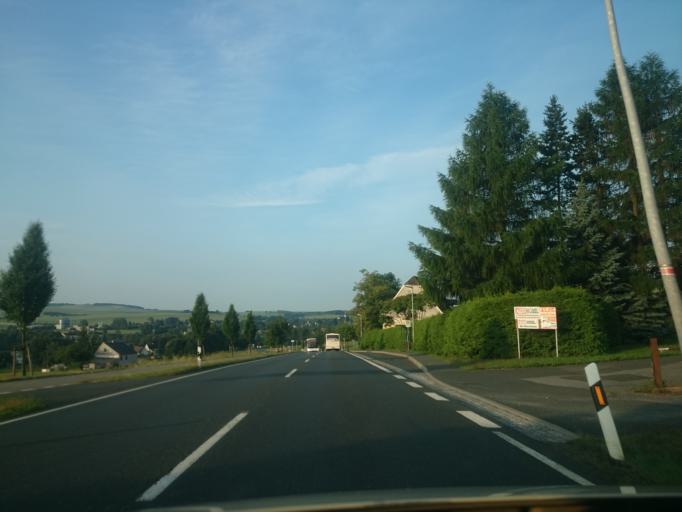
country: DE
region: Saxony
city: Grosshartmannsdorf
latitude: 50.8137
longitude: 13.3238
